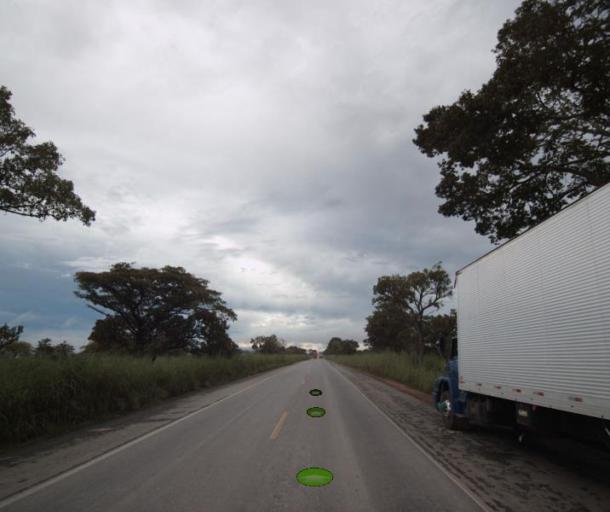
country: BR
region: Goias
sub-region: Porangatu
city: Porangatu
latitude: -13.5150
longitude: -49.1209
